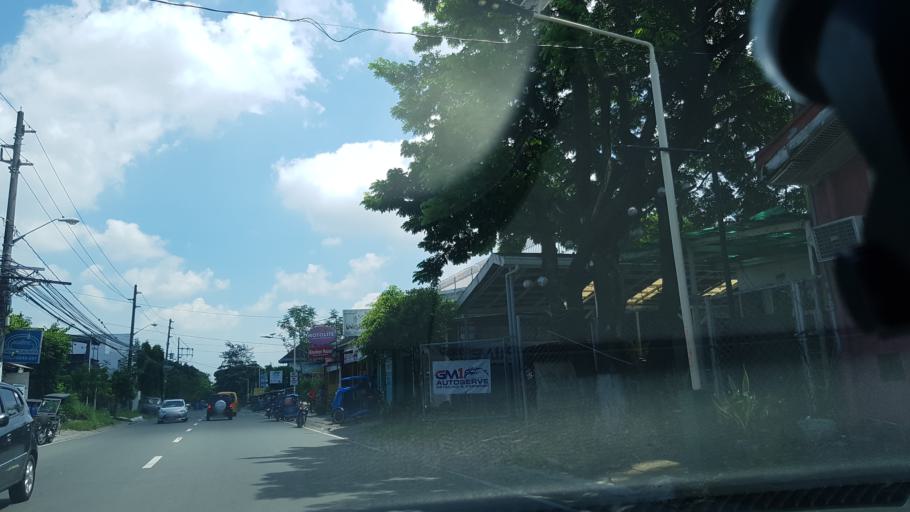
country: PH
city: Sambayanihan People's Village
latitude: 14.4512
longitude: 121.0037
